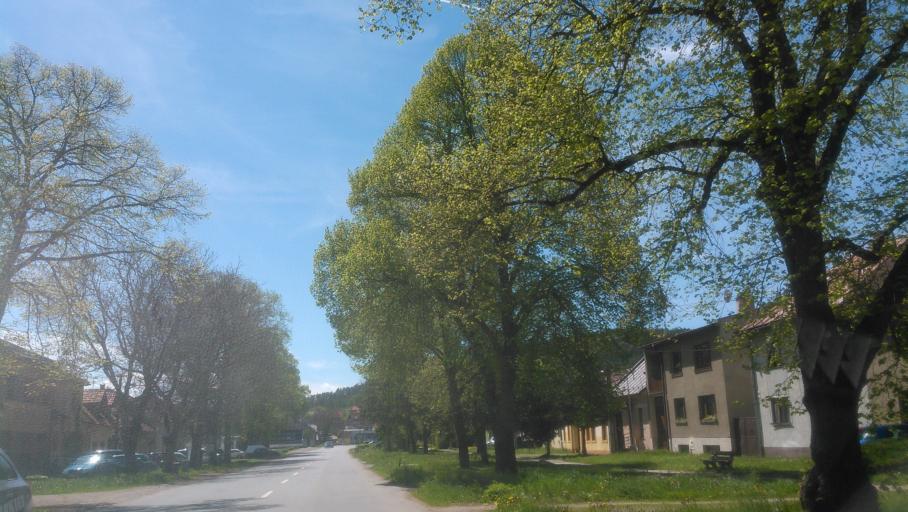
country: SK
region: Banskobystricky
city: Hrochot,Slovakia
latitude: 48.7663
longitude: 19.2713
